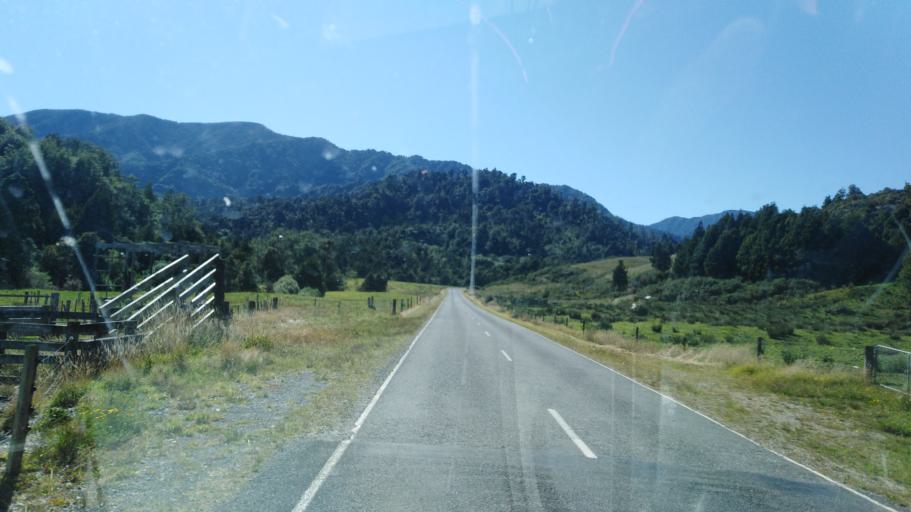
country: NZ
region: West Coast
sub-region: Buller District
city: Westport
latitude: -41.5295
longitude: 171.9835
